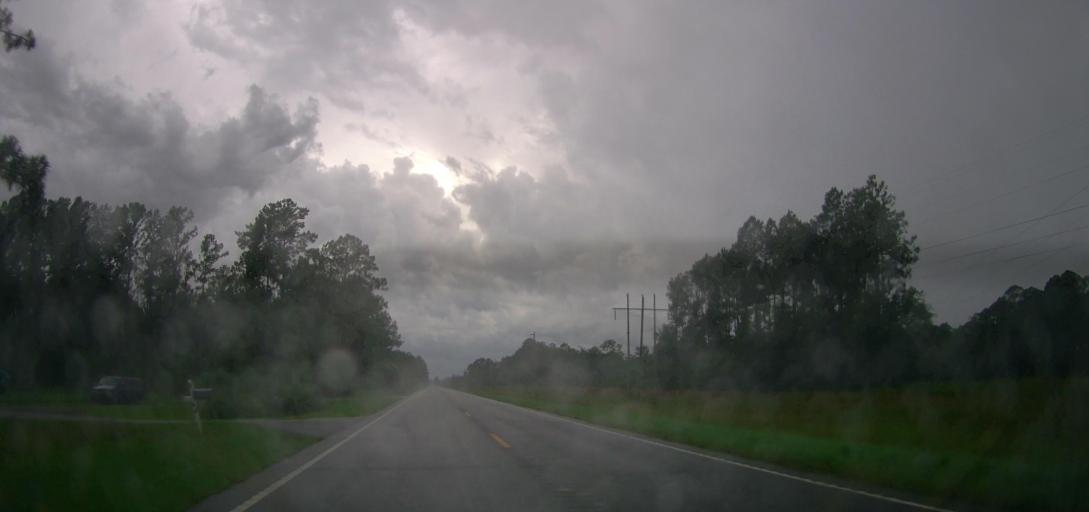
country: US
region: Georgia
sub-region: Brantley County
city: Nahunta
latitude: 31.3344
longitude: -81.8916
